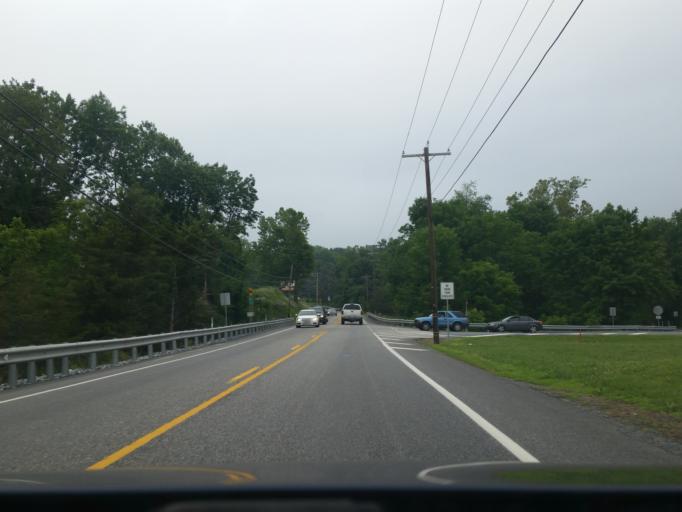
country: US
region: Pennsylvania
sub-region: Lebanon County
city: Annville
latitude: 40.3469
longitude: -76.5252
